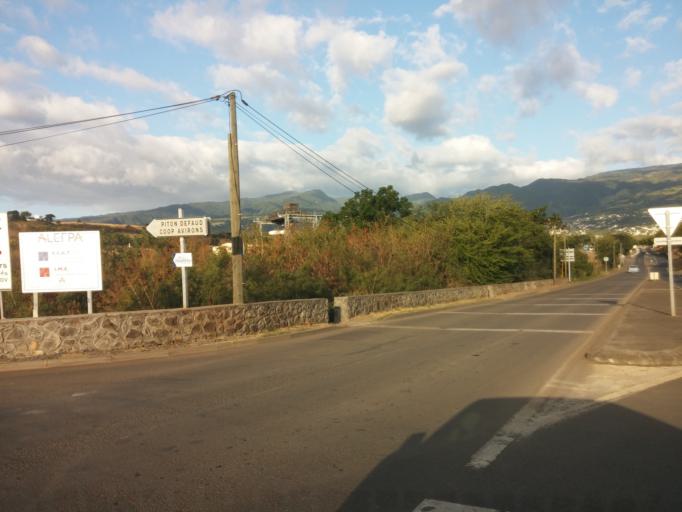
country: RE
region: Reunion
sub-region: Reunion
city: Le Port
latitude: -20.9713
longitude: 55.3001
